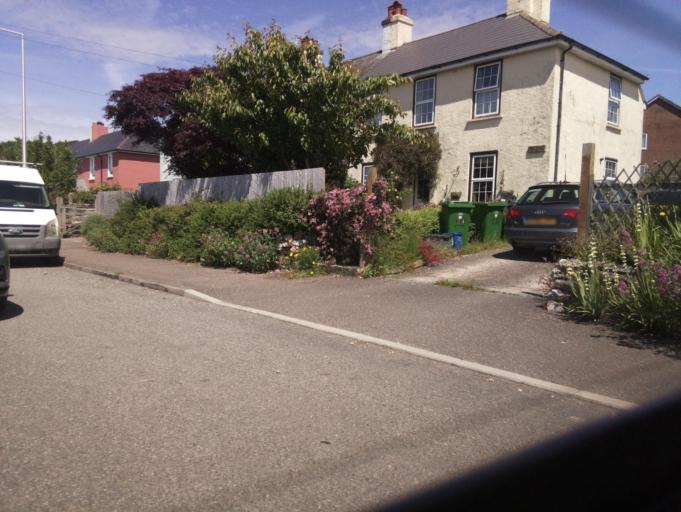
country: GB
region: England
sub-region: Devon
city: Honiton
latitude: 50.8009
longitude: -3.1961
